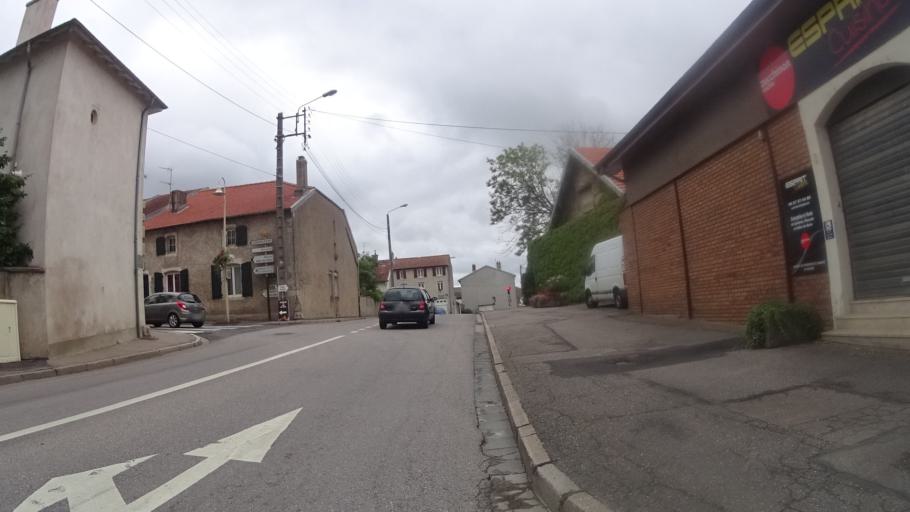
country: FR
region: Lorraine
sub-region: Departement de Meurthe-et-Moselle
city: Art-sur-Meurthe
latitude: 48.6561
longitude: 6.2643
